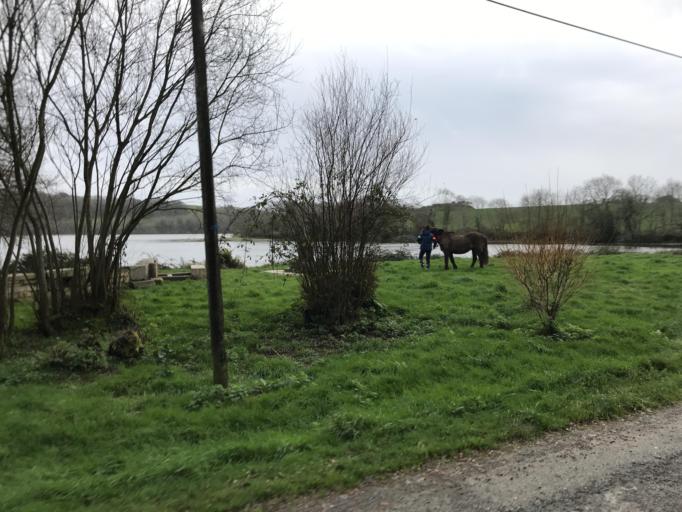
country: FR
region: Brittany
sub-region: Departement du Finistere
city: Daoulas
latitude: 48.3568
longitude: -4.2854
